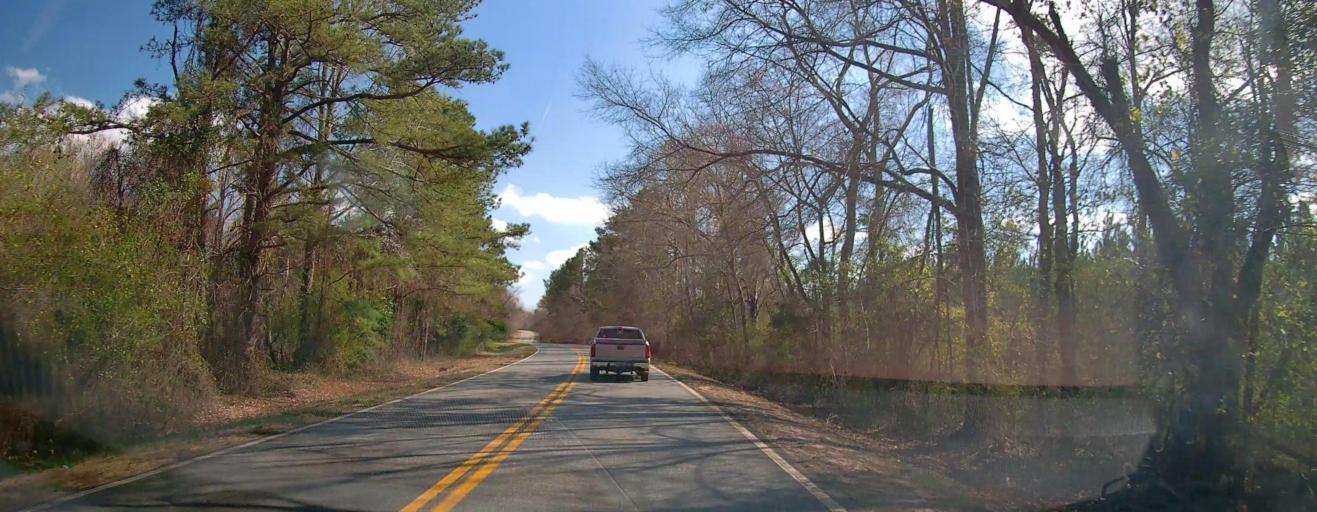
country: US
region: Georgia
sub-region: Twiggs County
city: Jeffersonville
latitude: 32.7002
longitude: -83.3495
